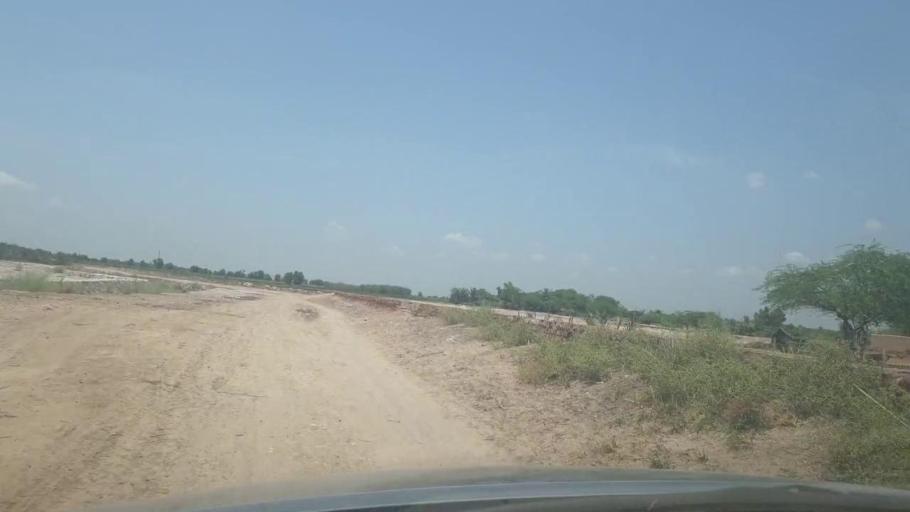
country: PK
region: Sindh
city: Kot Diji
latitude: 27.3869
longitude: 68.6971
